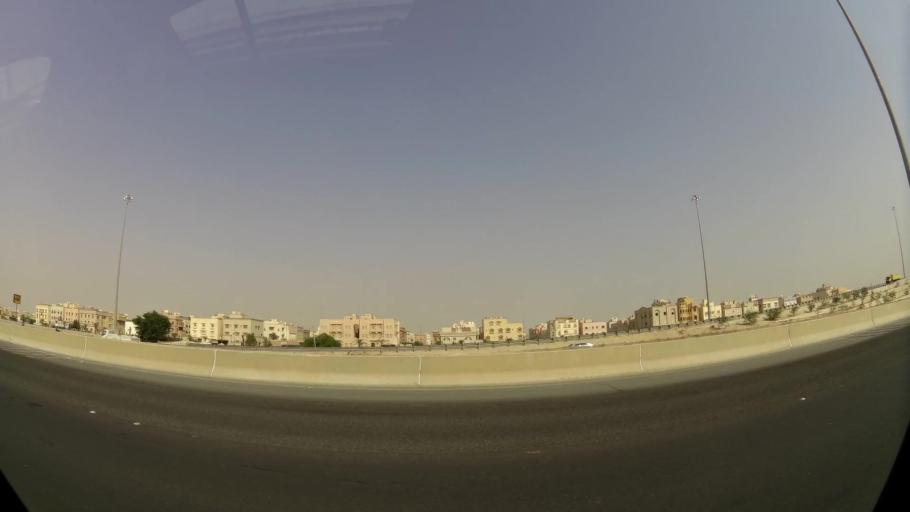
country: KW
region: Muhafazat al Jahra'
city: Al Jahra'
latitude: 29.2989
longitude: 47.7096
